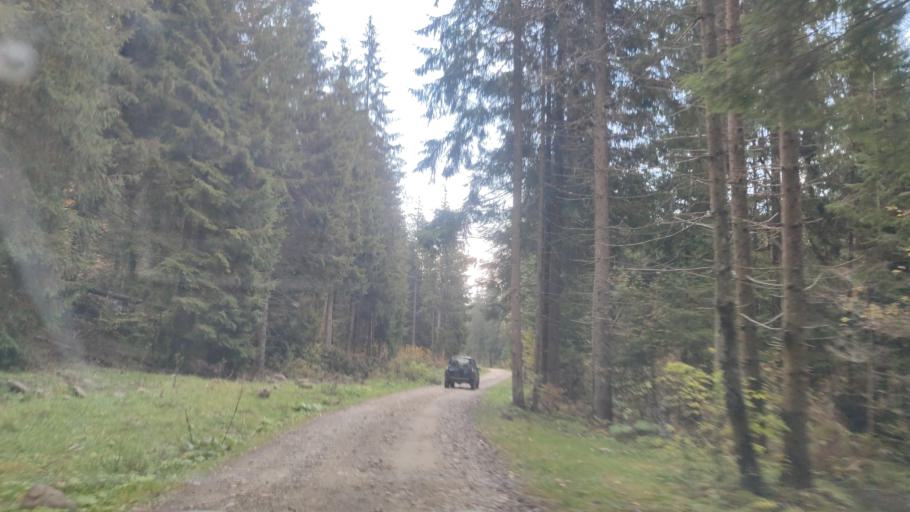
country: RO
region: Harghita
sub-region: Comuna Madaras
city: Madaras
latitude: 46.4800
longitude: 25.6563
